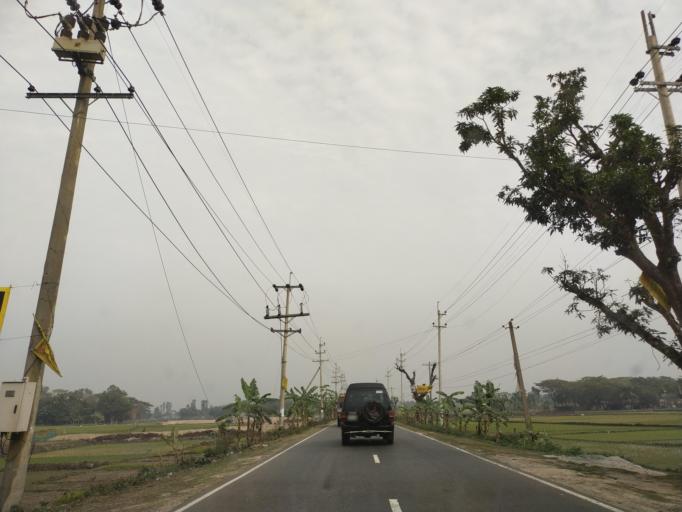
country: BD
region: Dhaka
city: Narsingdi
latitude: 23.9887
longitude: 90.7358
